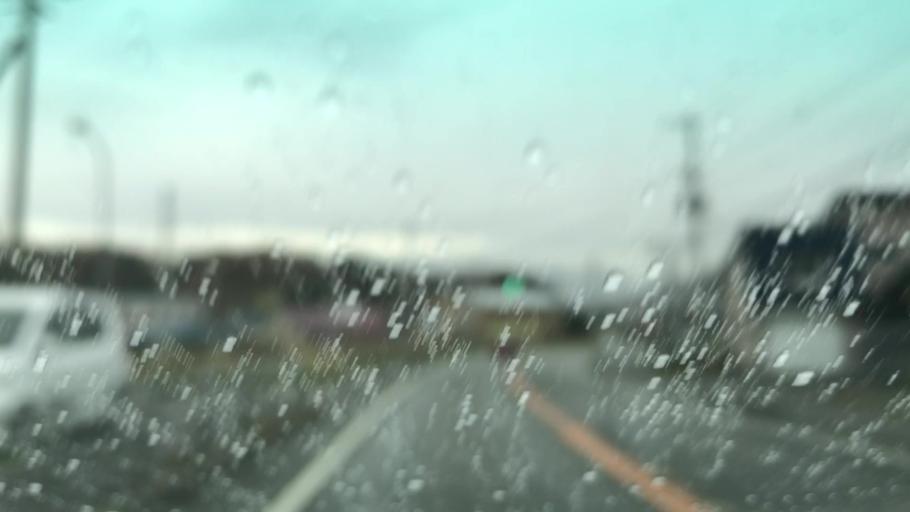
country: JP
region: Hokkaido
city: Shizunai-furukawacho
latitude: 42.2671
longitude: 142.4971
